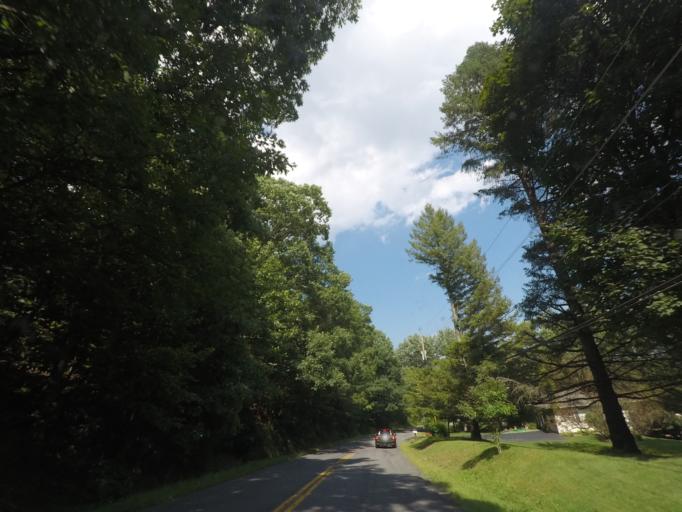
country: US
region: New York
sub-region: Saratoga County
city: Waterford
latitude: 42.8100
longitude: -73.6108
